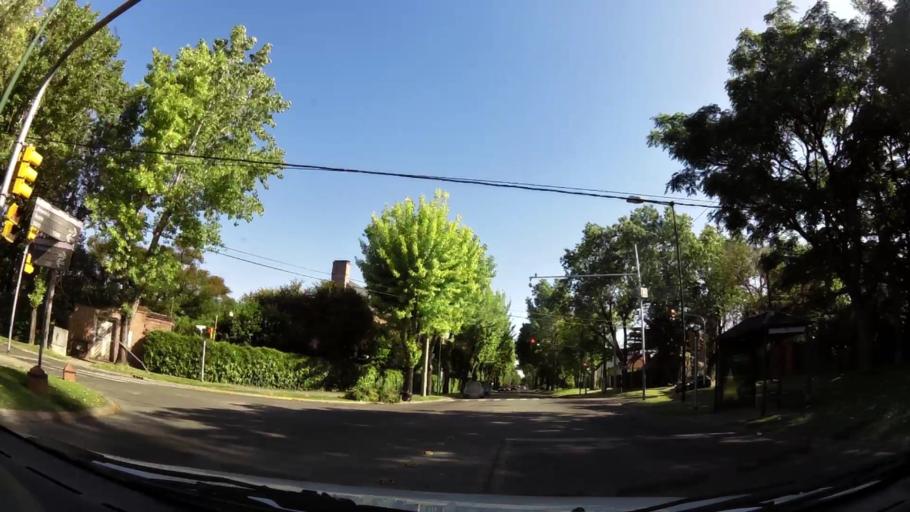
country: AR
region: Buenos Aires
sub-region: Partido de San Isidro
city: San Isidro
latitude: -34.4850
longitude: -58.5562
